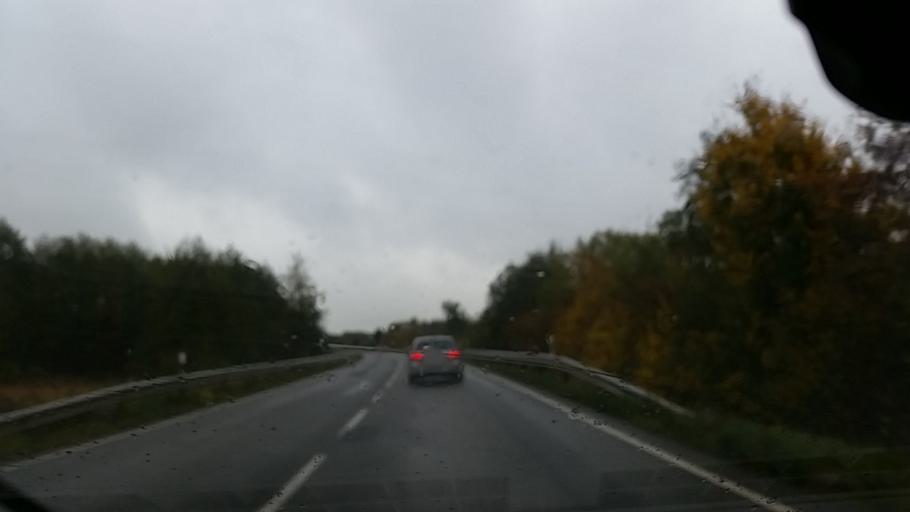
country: DE
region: Lower Saxony
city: Handorf
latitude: 53.3177
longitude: 10.3399
